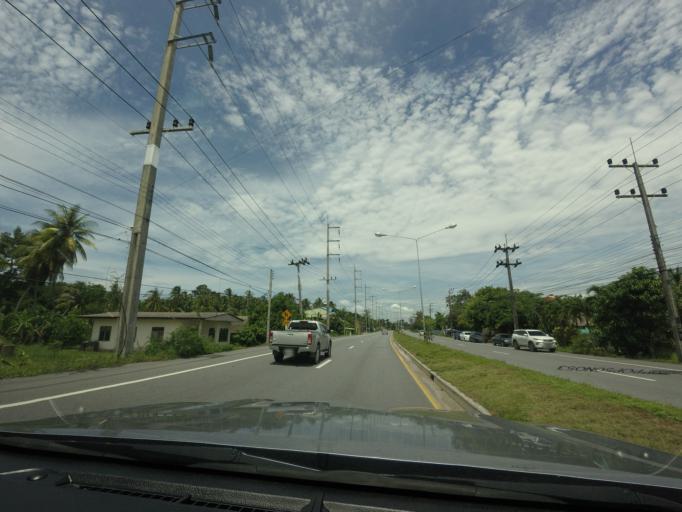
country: TH
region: Songkhla
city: Krasae Sin
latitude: 7.5776
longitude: 100.4086
